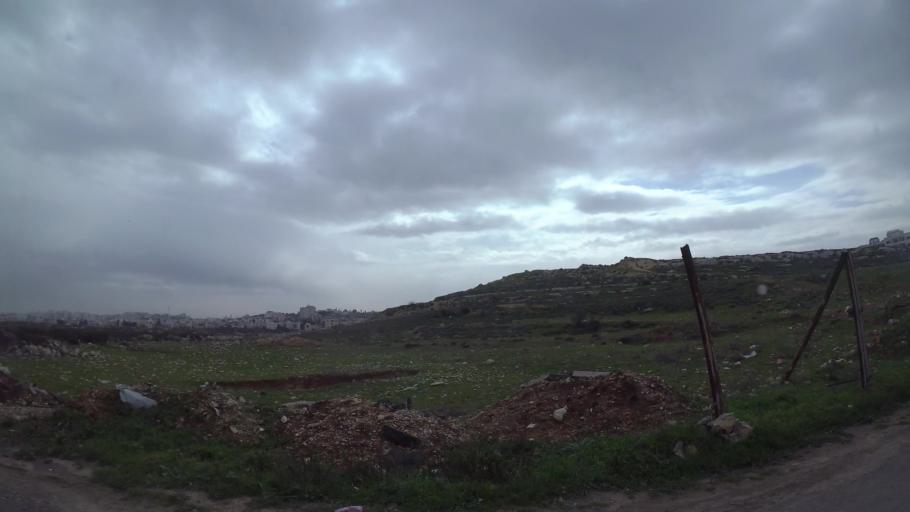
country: JO
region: Amman
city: Umm as Summaq
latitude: 31.8957
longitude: 35.8456
